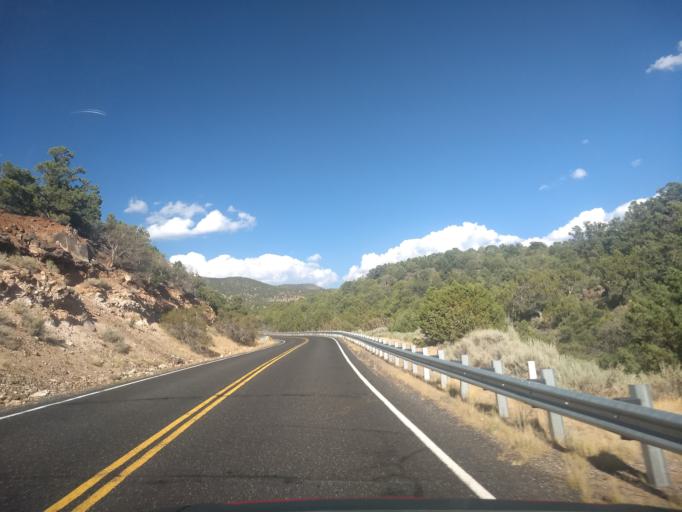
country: US
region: Utah
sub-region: Washington County
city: Enterprise
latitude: 37.4216
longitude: -113.5905
